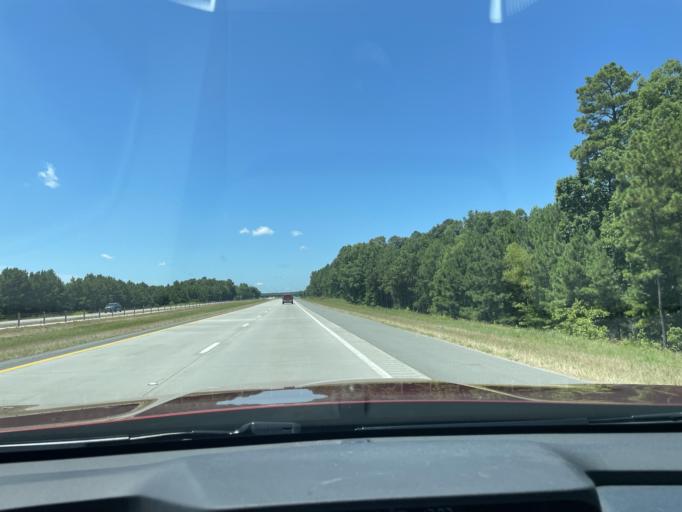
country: US
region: Arkansas
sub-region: Jefferson County
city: Pine Bluff
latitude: 34.1851
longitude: -91.9833
